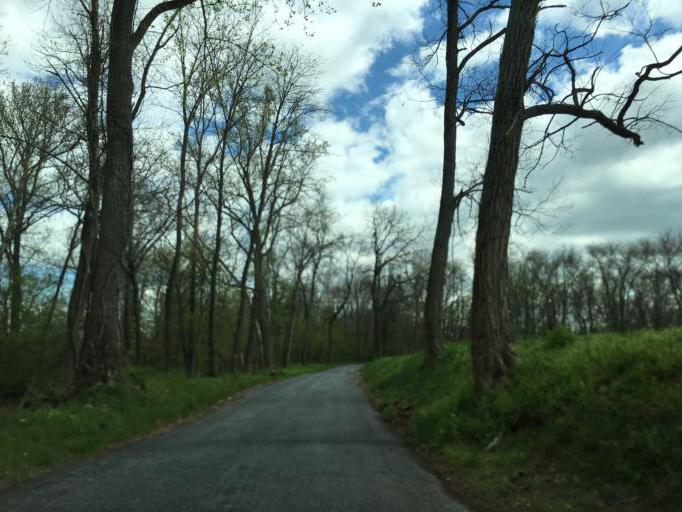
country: US
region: Maryland
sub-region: Frederick County
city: Thurmont
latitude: 39.5667
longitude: -77.3896
